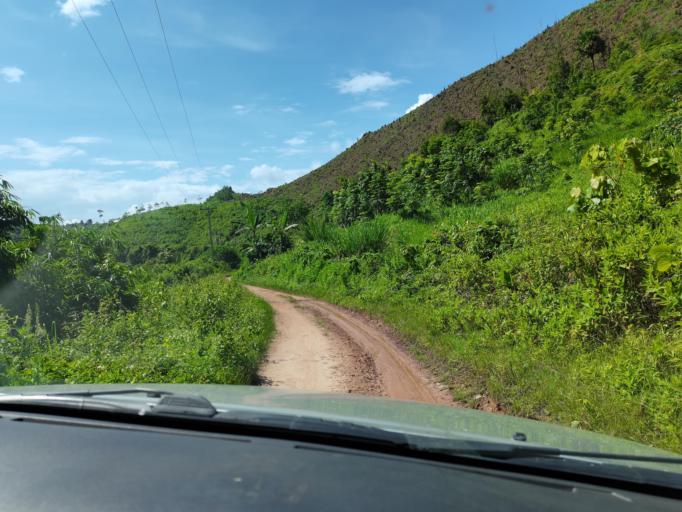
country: LA
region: Loungnamtha
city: Muang Nale
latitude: 20.5541
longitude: 101.0655
